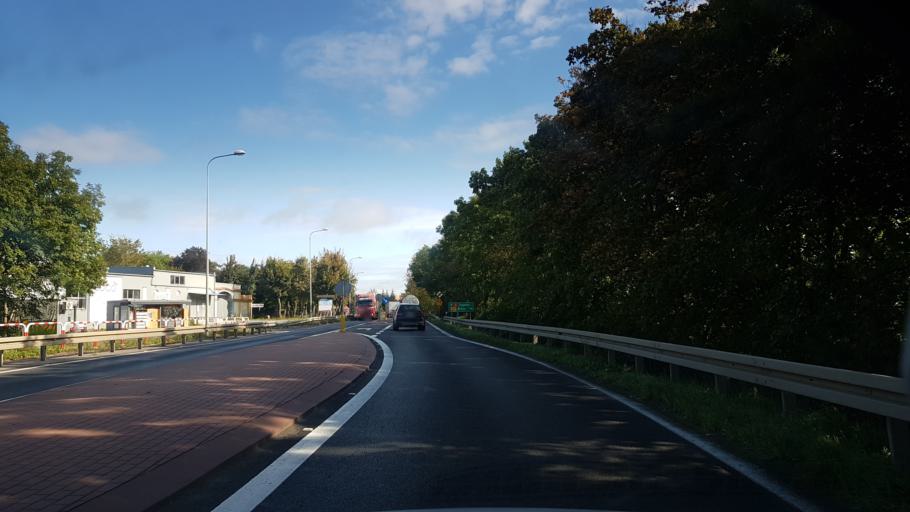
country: PL
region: Greater Poland Voivodeship
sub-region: Powiat koscianski
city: Czempin
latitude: 52.1753
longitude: 16.7085
